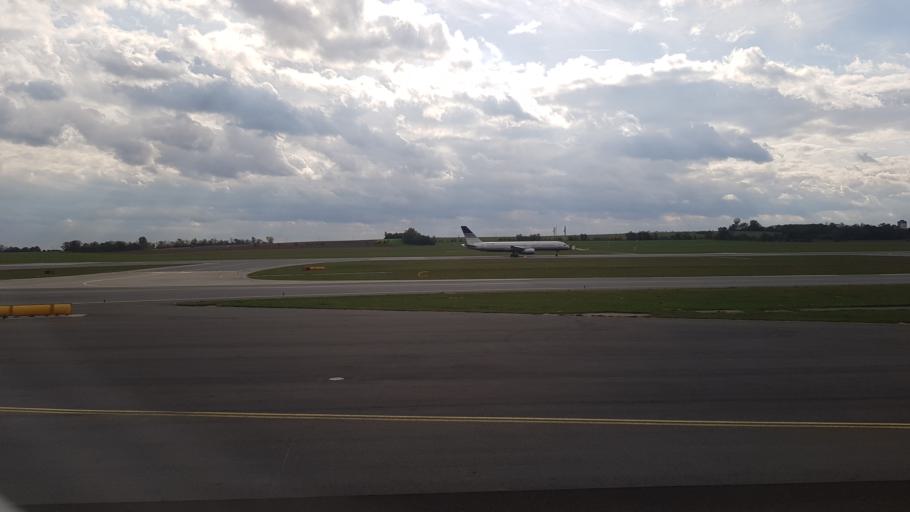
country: AT
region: Lower Austria
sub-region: Politischer Bezirk Bruck an der Leitha
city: Enzersdorf an der Fischa
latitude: 48.1122
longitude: 16.5754
